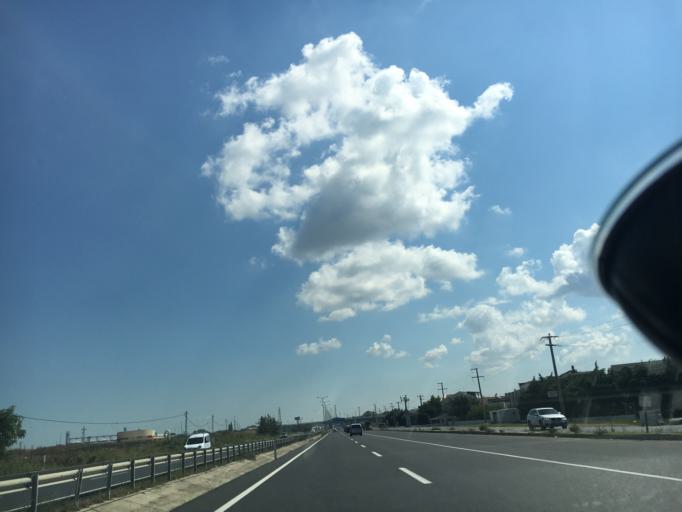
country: TR
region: Istanbul
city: Canta
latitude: 41.0652
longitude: 28.0995
